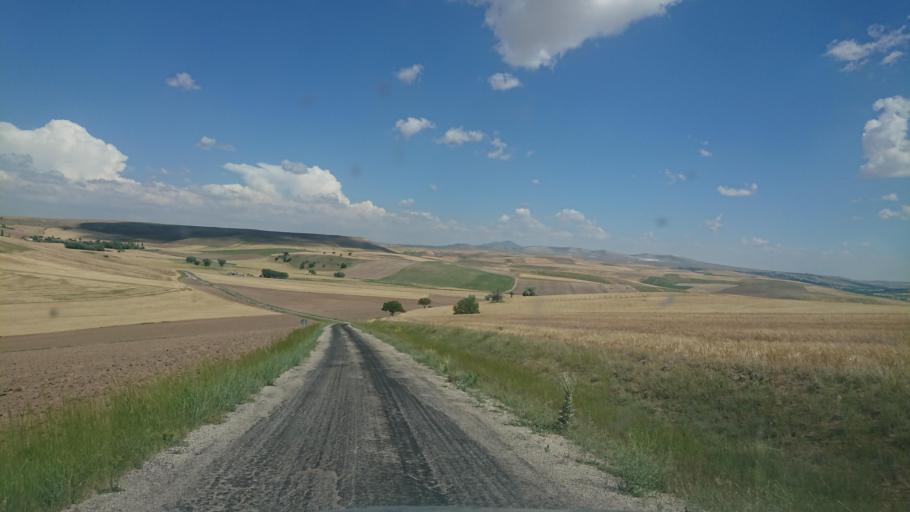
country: TR
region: Aksaray
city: Agacoren
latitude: 38.8013
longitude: 33.8153
